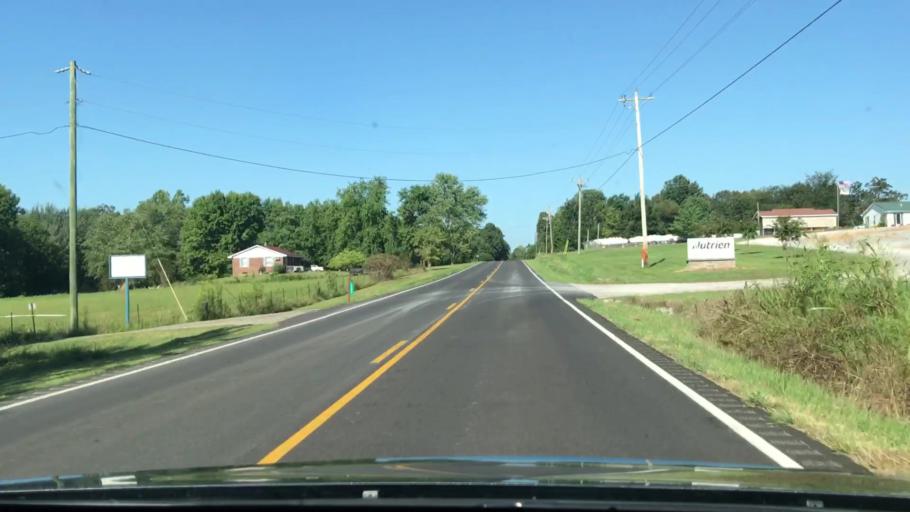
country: US
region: Kentucky
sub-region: Marshall County
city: Benton
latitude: 36.7647
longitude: -88.3263
